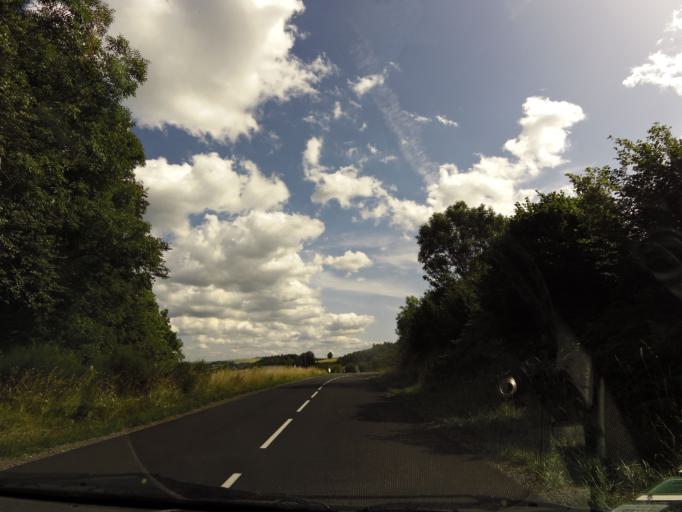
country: FR
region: Auvergne
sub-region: Departement du Puy-de-Dome
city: Aydat
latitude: 45.5449
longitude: 2.9432
